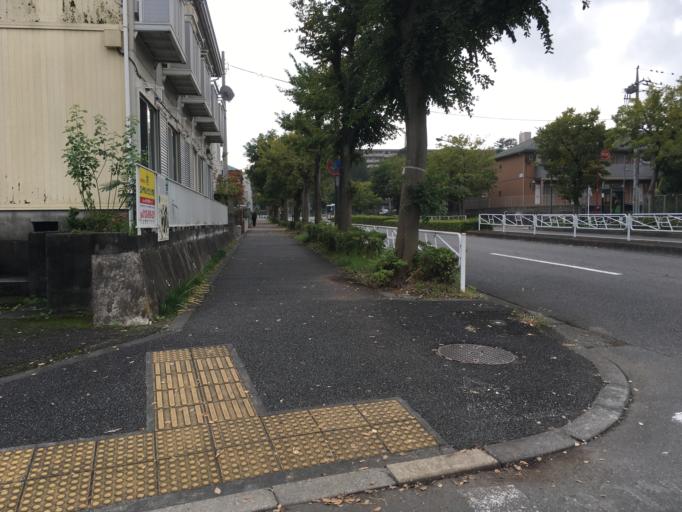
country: JP
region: Tokyo
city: Hino
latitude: 35.6123
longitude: 139.3825
